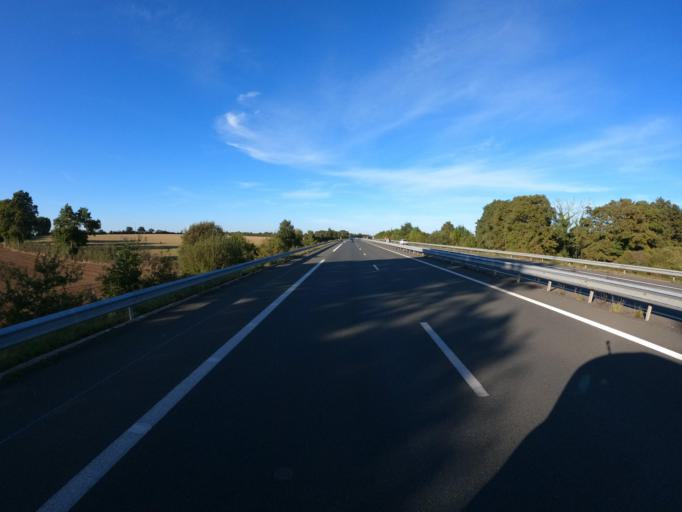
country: FR
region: Pays de la Loire
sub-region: Departement de Maine-et-Loire
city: Chemille-Melay
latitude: 47.1942
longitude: -0.7748
